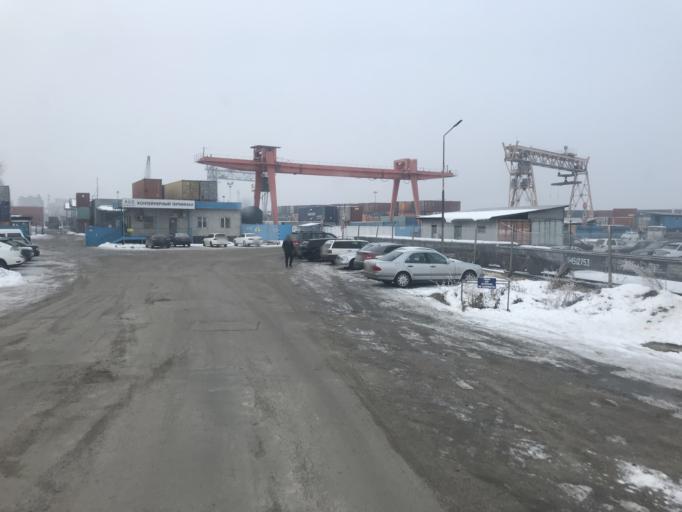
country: KZ
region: Almaty Oblysy
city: Pervomayskiy
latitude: 43.3584
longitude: 76.9733
